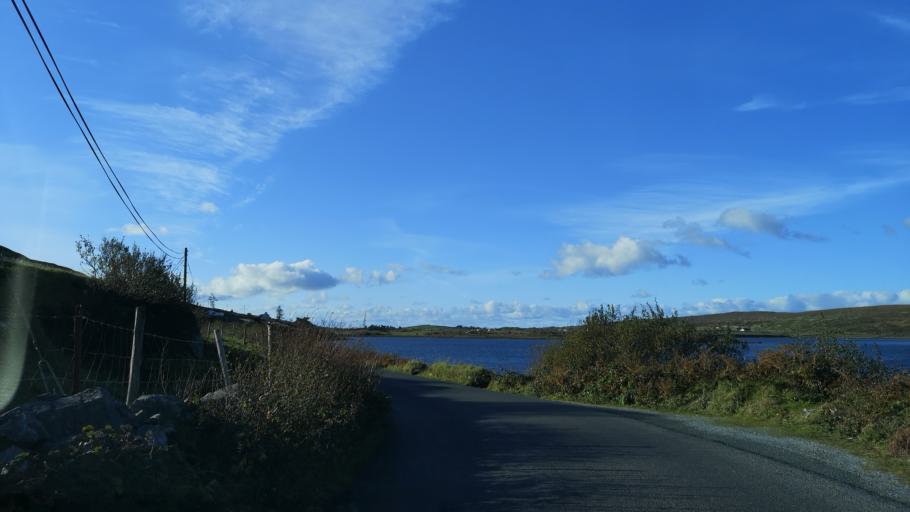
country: IE
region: Connaught
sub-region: County Galway
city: Clifden
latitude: 53.5041
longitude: -10.0647
